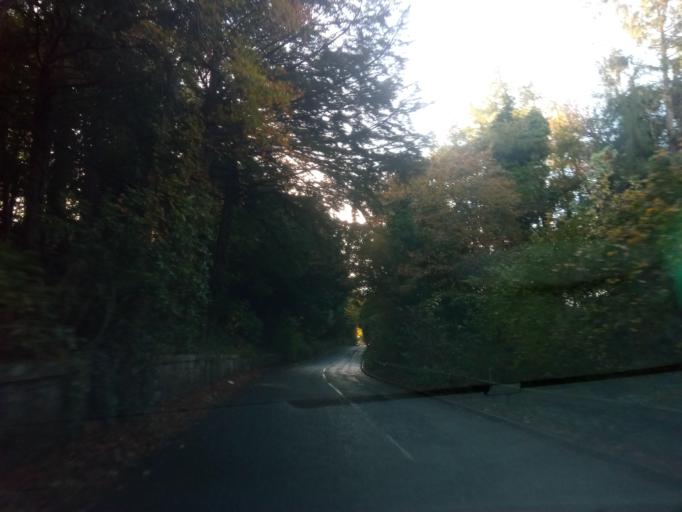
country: GB
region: Scotland
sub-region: The Scottish Borders
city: Eyemouth
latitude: 55.8487
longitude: -2.1112
